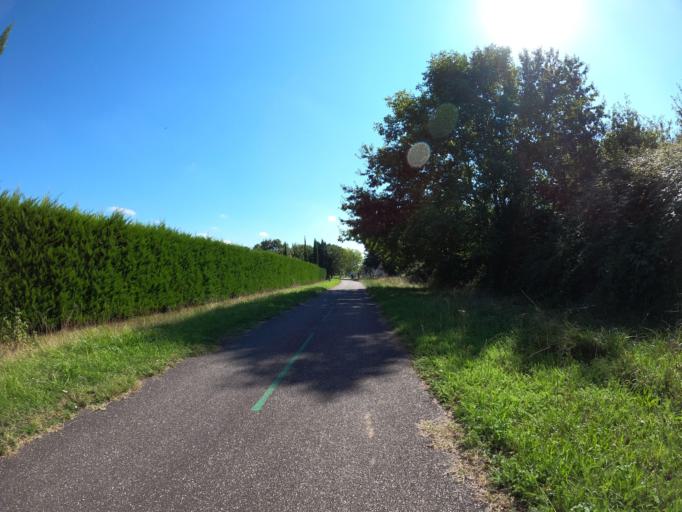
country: FR
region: Aquitaine
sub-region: Departement du Lot-et-Garonne
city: Bias
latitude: 44.4224
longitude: 0.6536
